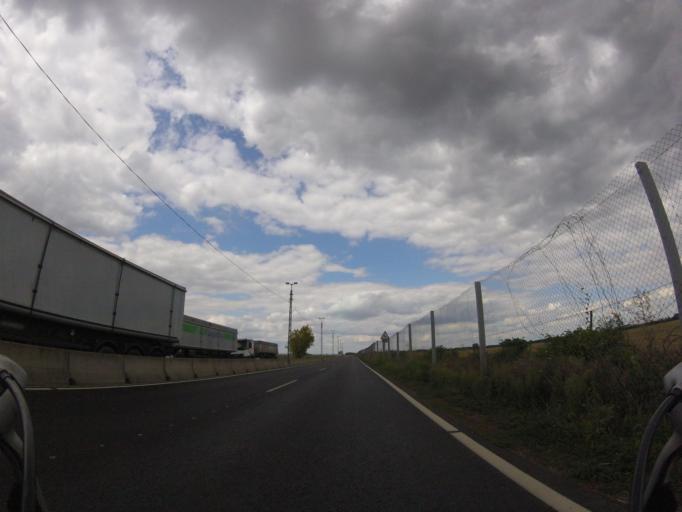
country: HU
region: Baranya
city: Mohacs
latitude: 45.9061
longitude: 18.6598
